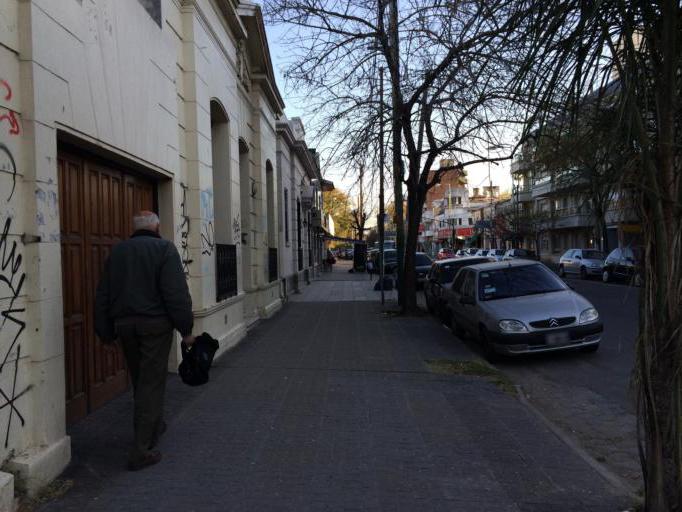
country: AR
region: Buenos Aires
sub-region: Partido de Lomas de Zamora
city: Lomas de Zamora
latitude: -34.7421
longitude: -58.3958
